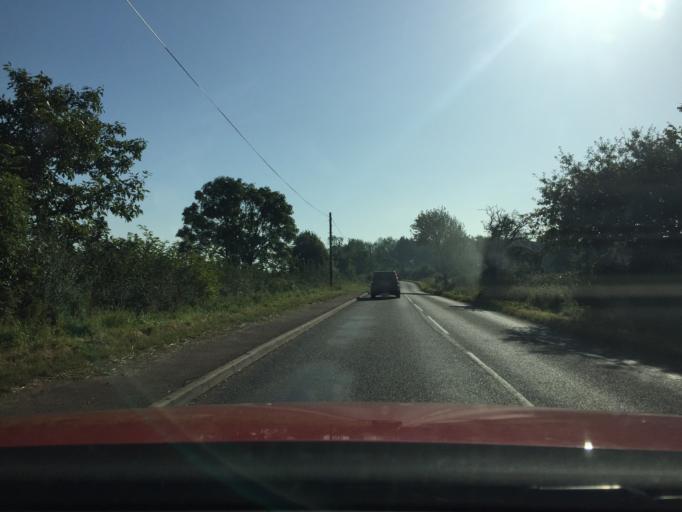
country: GB
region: England
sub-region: Leicestershire
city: Syston
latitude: 52.6791
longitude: -1.0547
